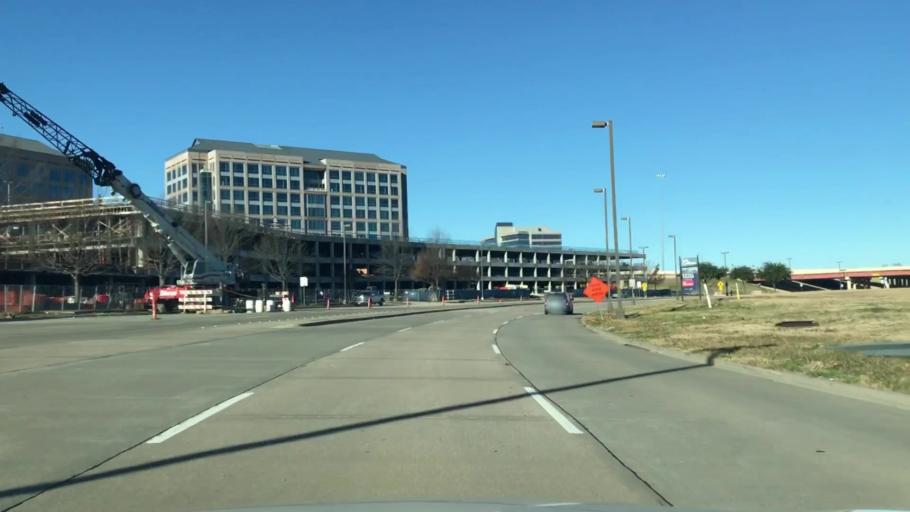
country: US
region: Texas
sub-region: Dallas County
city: Farmers Branch
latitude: 32.8960
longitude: -96.9658
